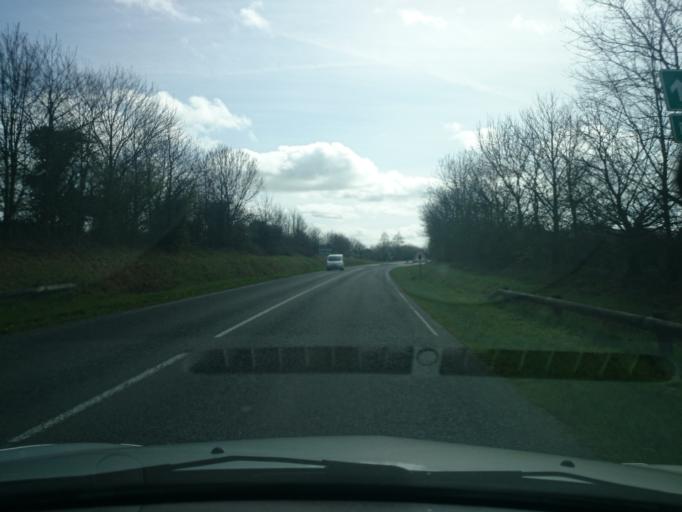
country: FR
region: Brittany
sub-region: Departement du Finistere
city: Gouesnou
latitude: 48.4363
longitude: -4.4469
